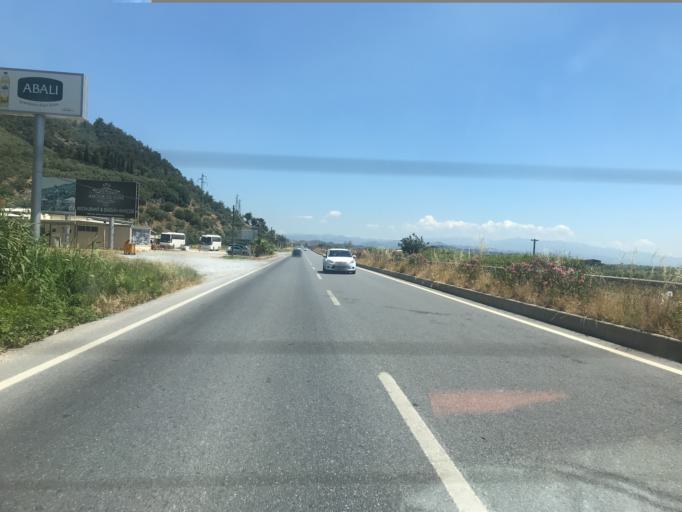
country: TR
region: Aydin
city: Soeke
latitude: 37.8020
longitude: 27.4743
